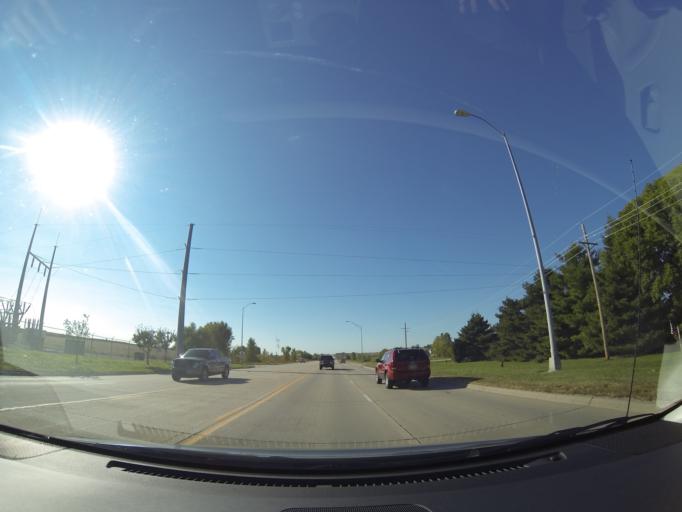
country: US
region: Nebraska
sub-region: Sarpy County
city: Gretna
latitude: 41.1257
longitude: -96.2534
